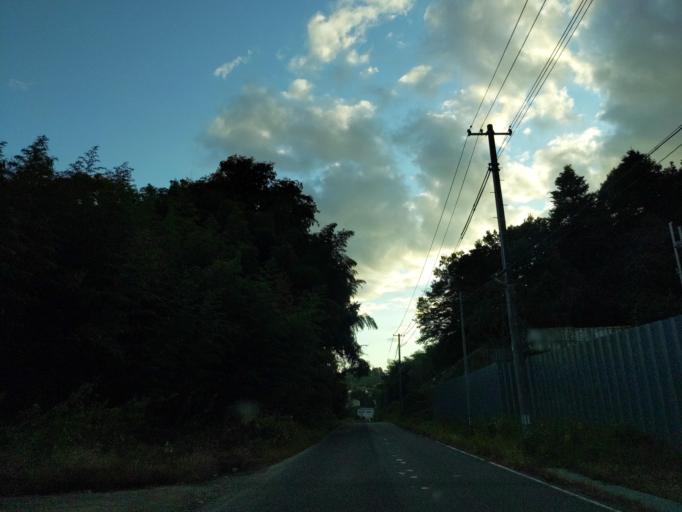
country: JP
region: Fukushima
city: Motomiya
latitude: 37.4777
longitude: 140.4386
